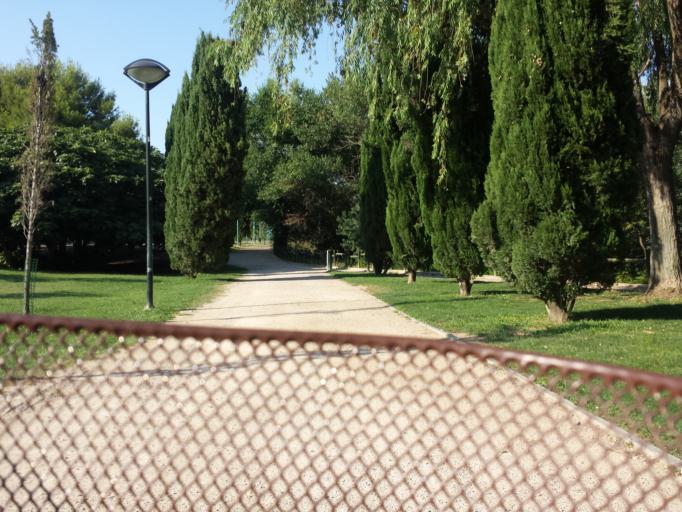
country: ES
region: Aragon
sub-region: Provincia de Zaragoza
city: Zaragoza
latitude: 41.6509
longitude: -0.8662
